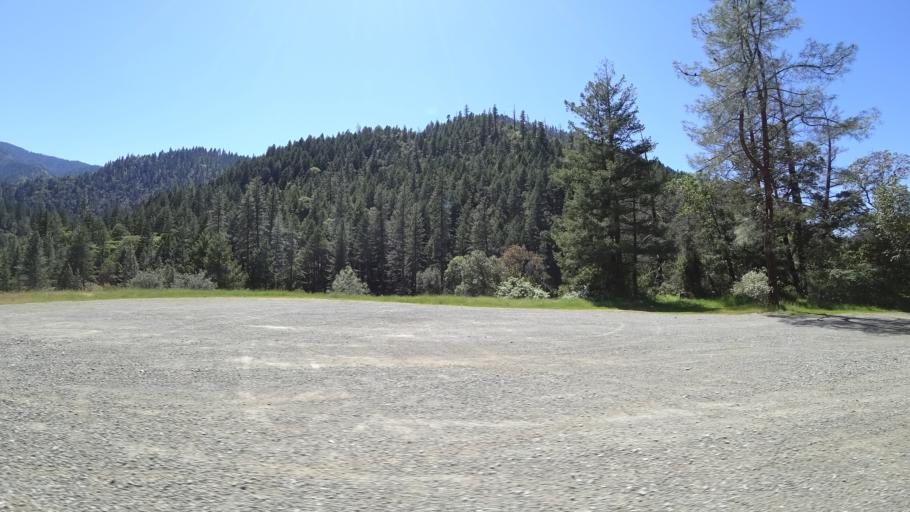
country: US
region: California
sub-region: Trinity County
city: Hayfork
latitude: 40.7915
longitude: -123.3501
